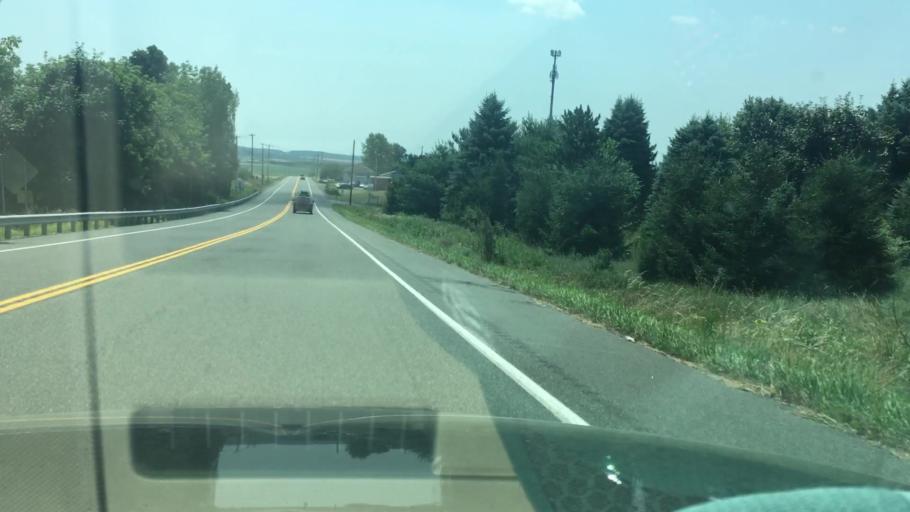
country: US
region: Pennsylvania
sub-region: Lehigh County
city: Schnecksville
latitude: 40.6481
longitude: -75.6836
